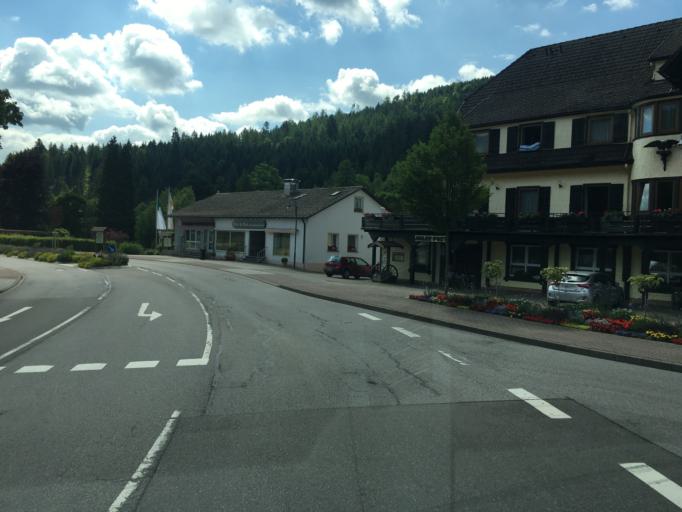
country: DE
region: Baden-Wuerttemberg
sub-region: Karlsruhe Region
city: Biberach
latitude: 48.5332
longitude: 8.2888
